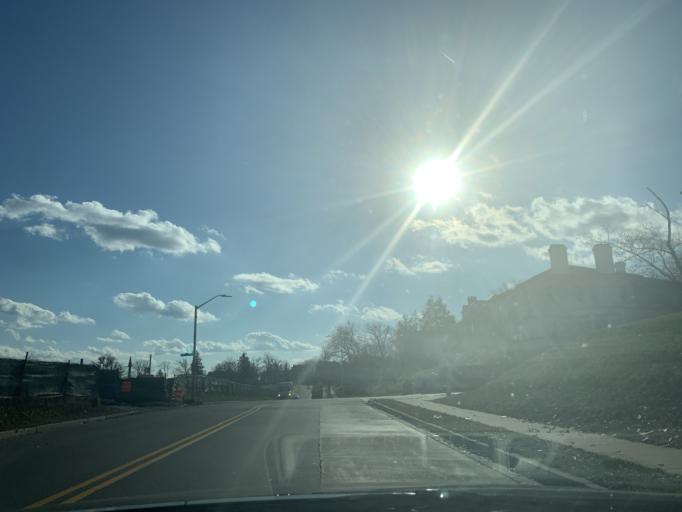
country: US
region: Maryland
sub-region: Baltimore County
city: Lochearn
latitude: 39.3236
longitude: -76.6718
